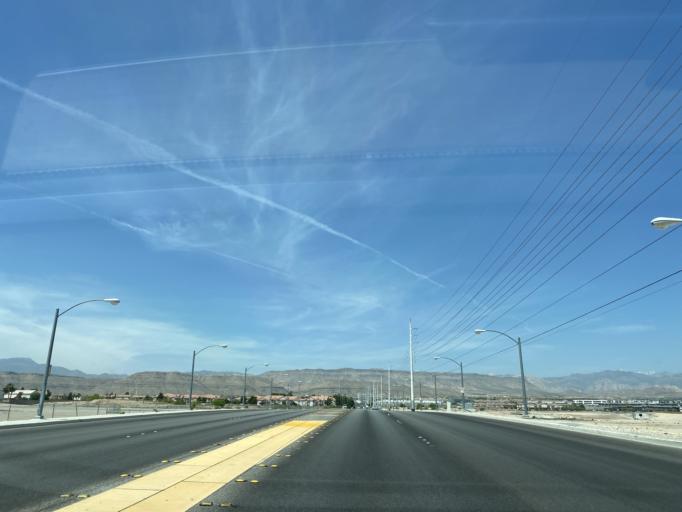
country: US
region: Nevada
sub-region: Clark County
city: Spring Valley
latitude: 36.0851
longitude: -115.2702
